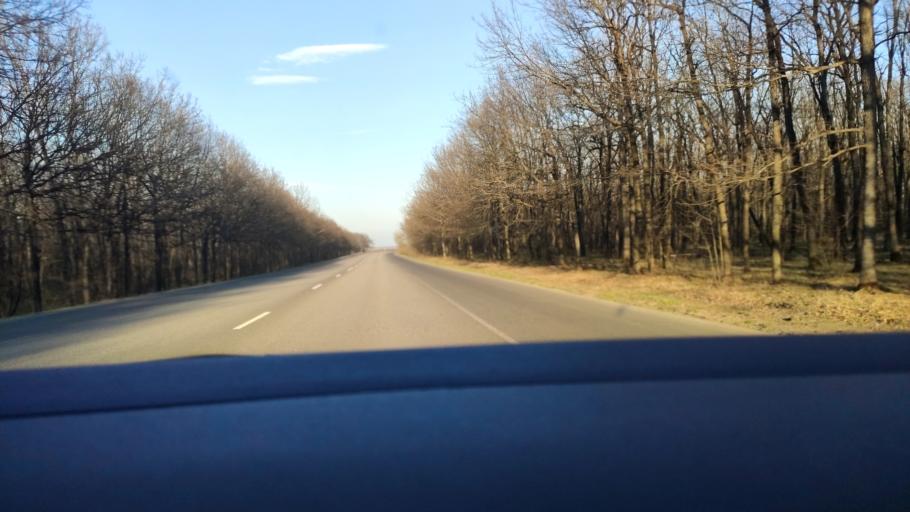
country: RU
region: Voronezj
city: Kolodeznyy
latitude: 51.3393
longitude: 39.0662
